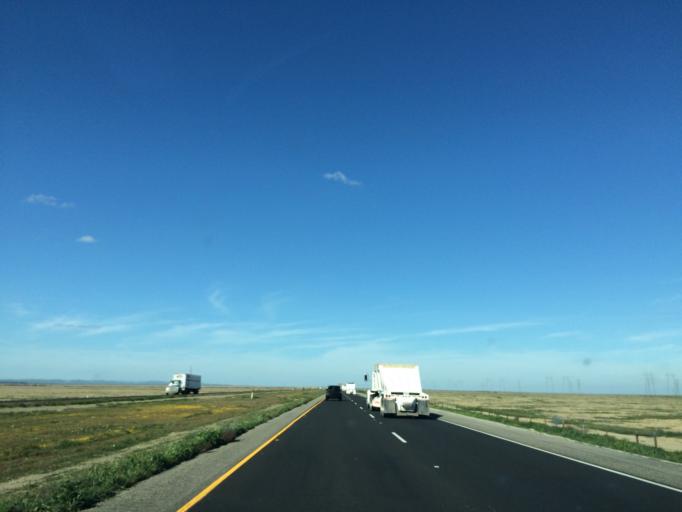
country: US
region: California
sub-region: Kern County
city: Lost Hills
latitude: 35.8225
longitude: -119.8067
